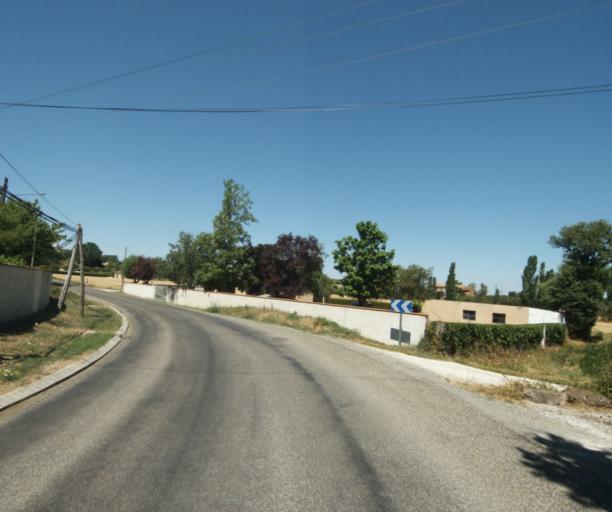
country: FR
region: Midi-Pyrenees
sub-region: Departement de la Haute-Garonne
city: Saint-Felix-Lauragais
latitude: 43.4728
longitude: 1.9305
